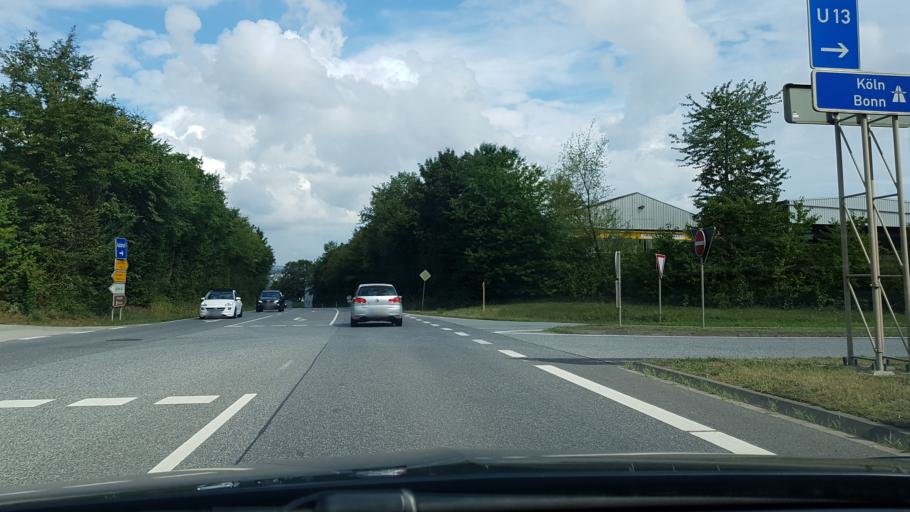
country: DE
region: Rheinland-Pfalz
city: Plaidt
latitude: 50.3793
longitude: 7.3868
